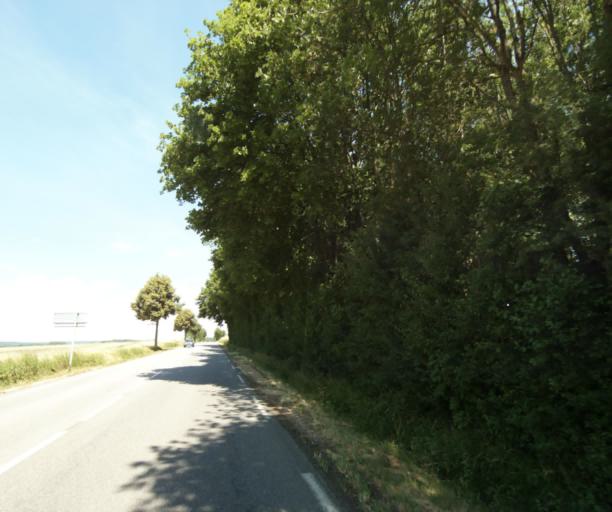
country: FR
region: Lorraine
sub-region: Departement de Meurthe-et-Moselle
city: Luneville
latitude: 48.6151
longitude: 6.4875
